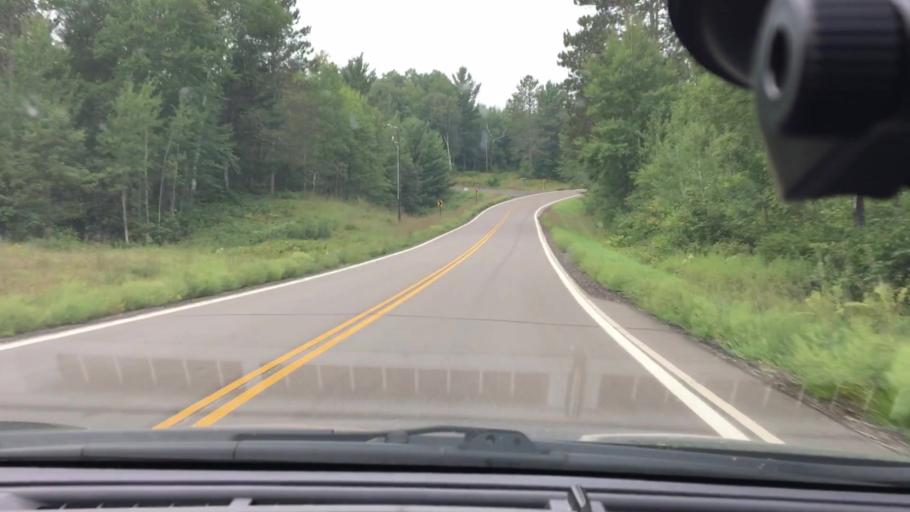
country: US
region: Minnesota
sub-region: Crow Wing County
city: Cross Lake
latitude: 46.6597
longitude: -93.9657
